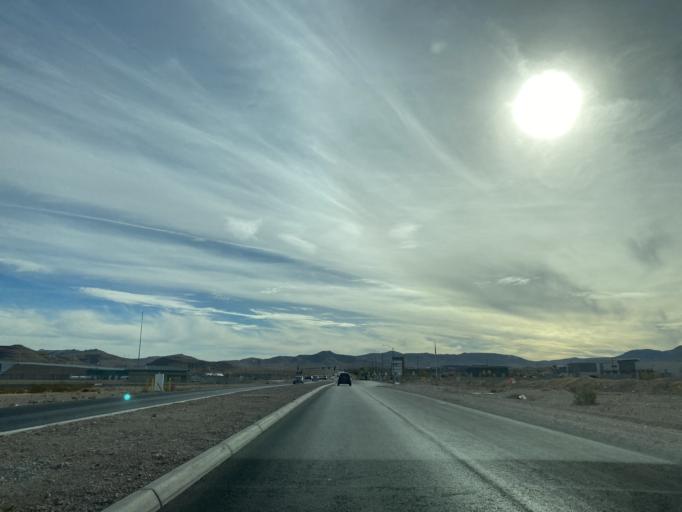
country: US
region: Nevada
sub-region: Clark County
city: Enterprise
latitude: 36.0019
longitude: -115.2436
